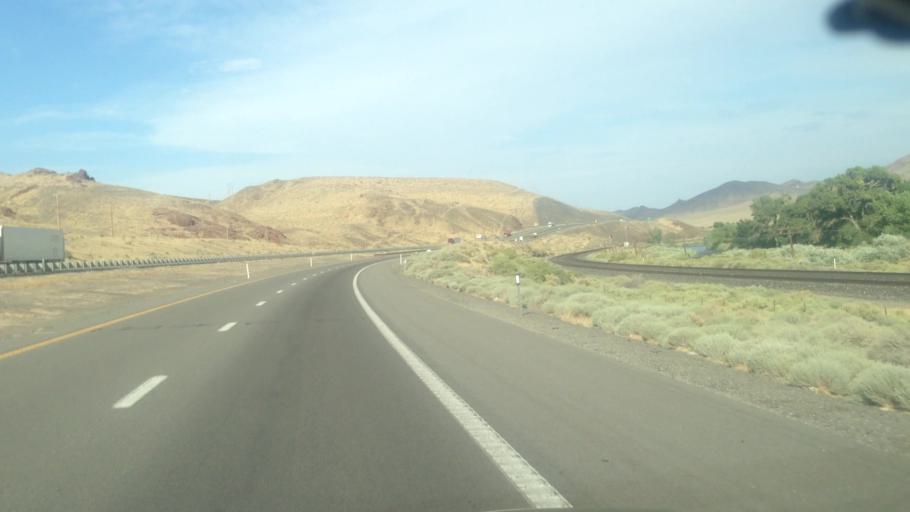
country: US
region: Nevada
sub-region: Lyon County
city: Fernley
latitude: 39.5910
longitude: -119.4161
